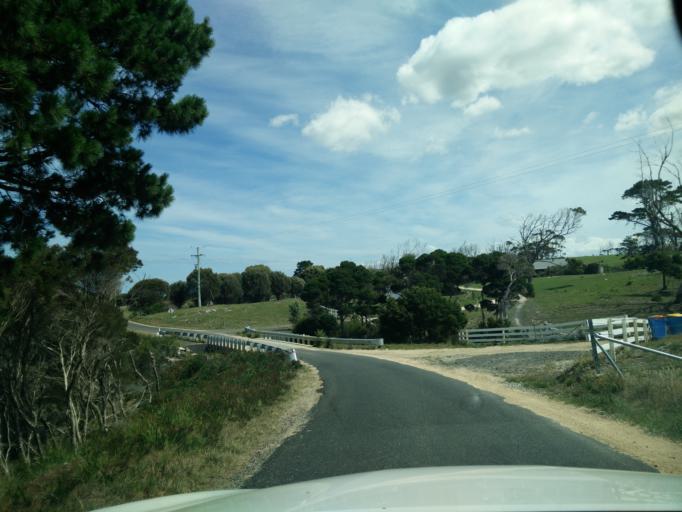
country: AU
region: Tasmania
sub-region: Break O'Day
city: St Helens
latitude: -41.1701
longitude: 148.2793
